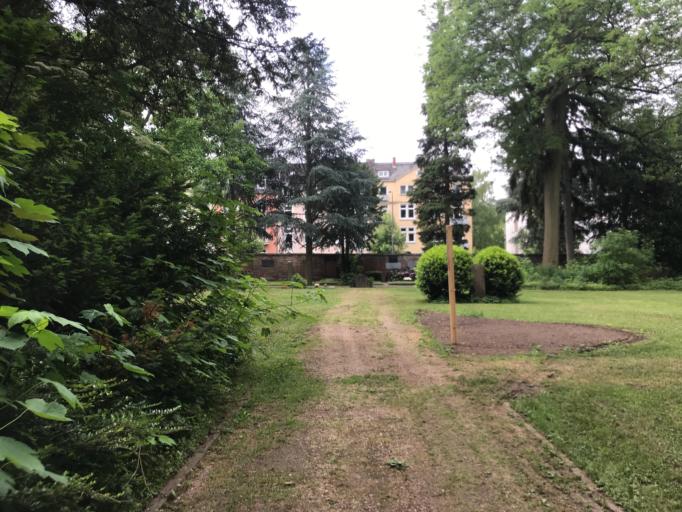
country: DE
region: Hesse
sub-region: Regierungsbezirk Darmstadt
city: Frankfurt am Main
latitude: 50.1325
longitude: 8.6874
